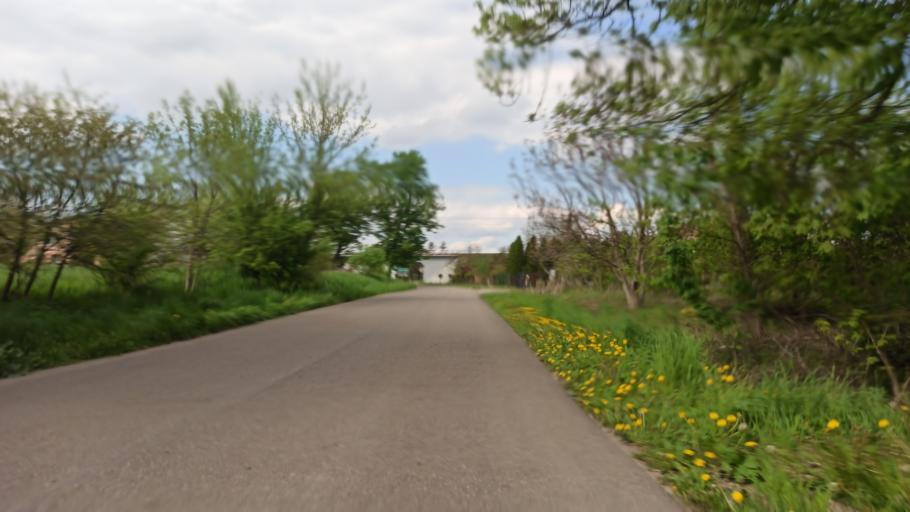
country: PL
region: Subcarpathian Voivodeship
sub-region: Powiat jaroslawski
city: Radymno
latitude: 49.9431
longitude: 22.8136
